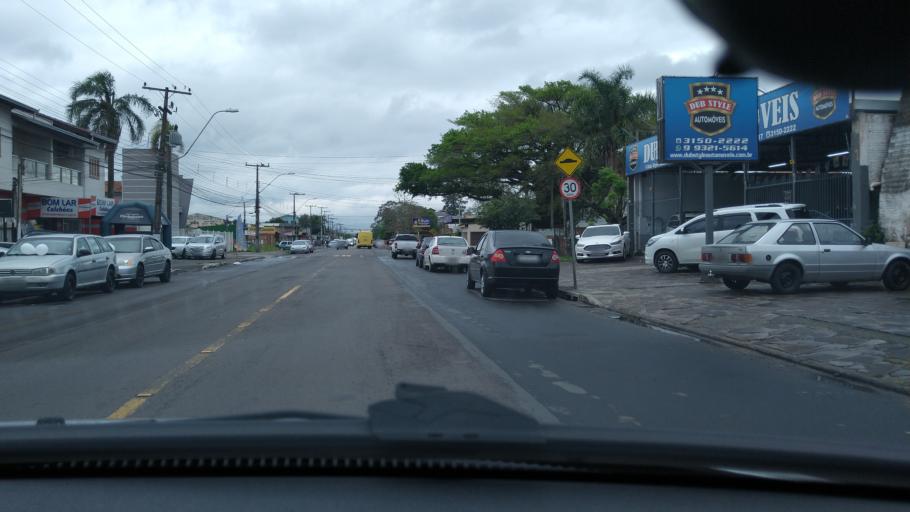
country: BR
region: Rio Grande do Sul
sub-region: Canoas
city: Canoas
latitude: -29.9017
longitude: -51.2104
